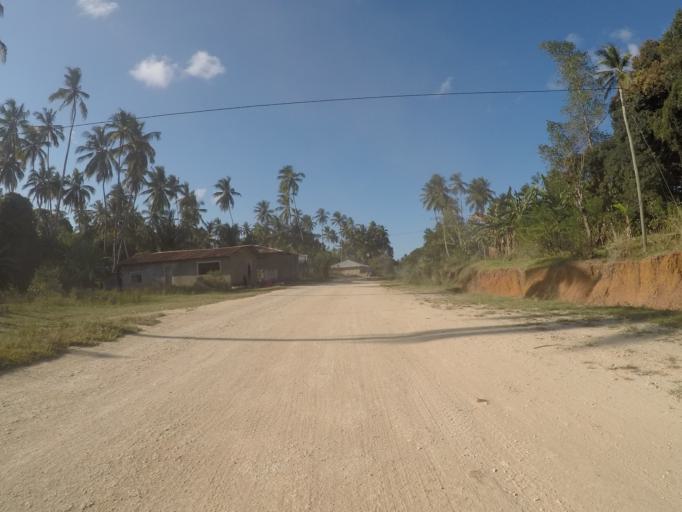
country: TZ
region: Zanzibar Central/South
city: Koani
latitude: -6.1764
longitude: 39.2834
